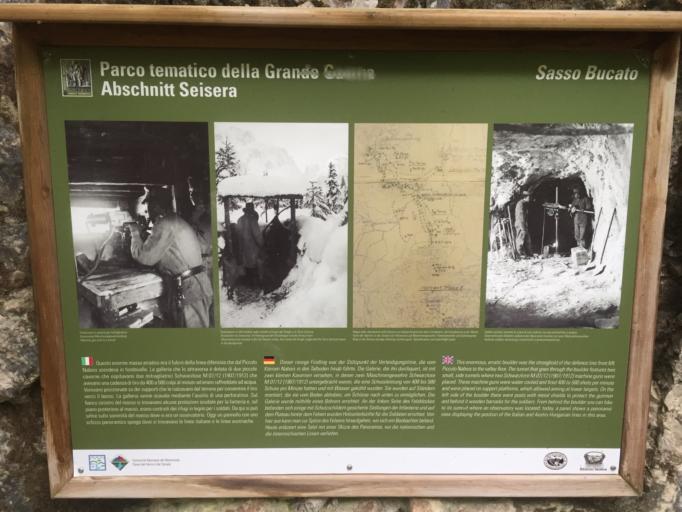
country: IT
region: Friuli Venezia Giulia
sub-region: Provincia di Udine
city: Malborghetto
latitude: 46.4564
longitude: 13.4874
